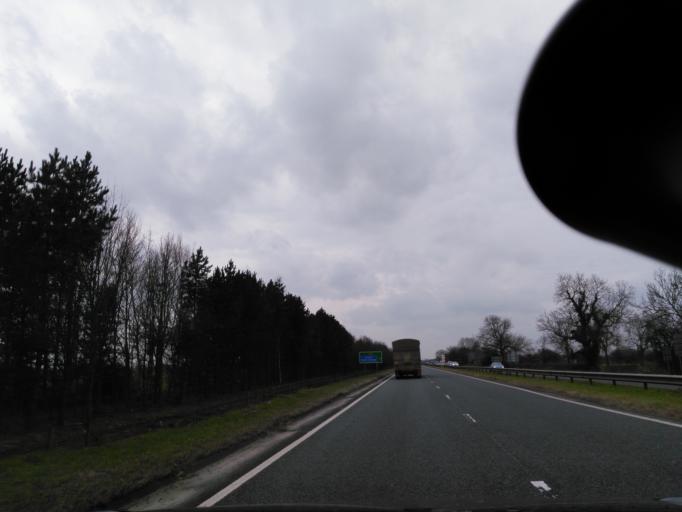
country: GB
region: England
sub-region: North Yorkshire
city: Thirsk
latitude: 54.2009
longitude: -1.3599
